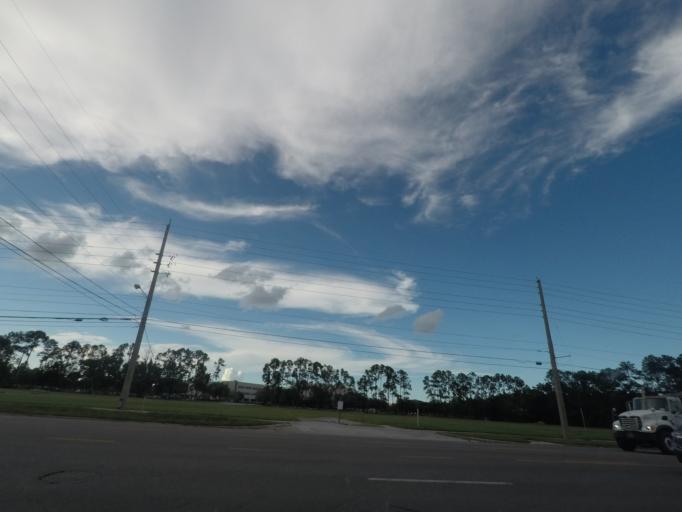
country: US
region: Florida
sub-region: Orange County
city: Oak Ridge
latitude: 28.5087
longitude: -81.4238
